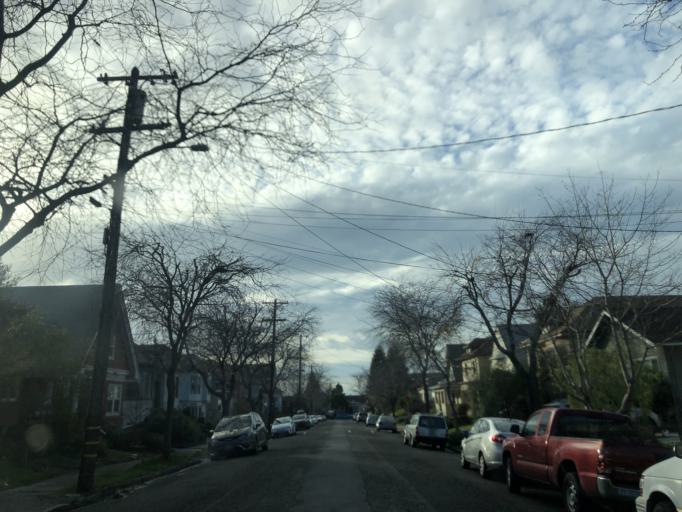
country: US
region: California
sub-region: Alameda County
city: Berkeley
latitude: 37.8481
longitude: -122.2633
